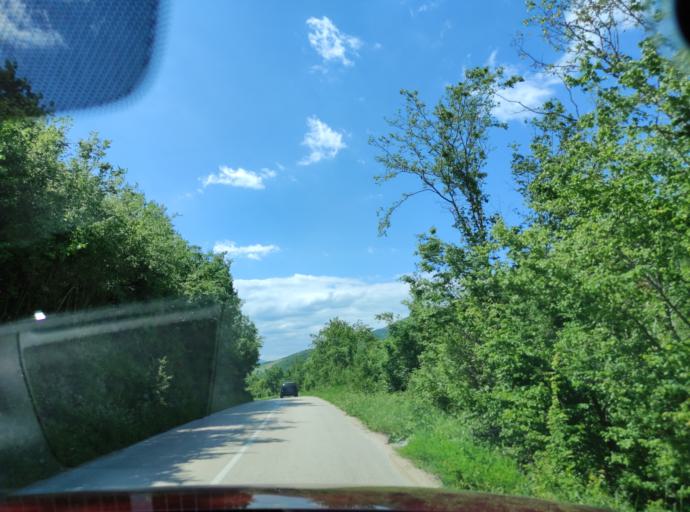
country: BG
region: Vidin
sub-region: Obshtina Ruzhintsi
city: Ruzhintsi
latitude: 43.4935
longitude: 22.7958
